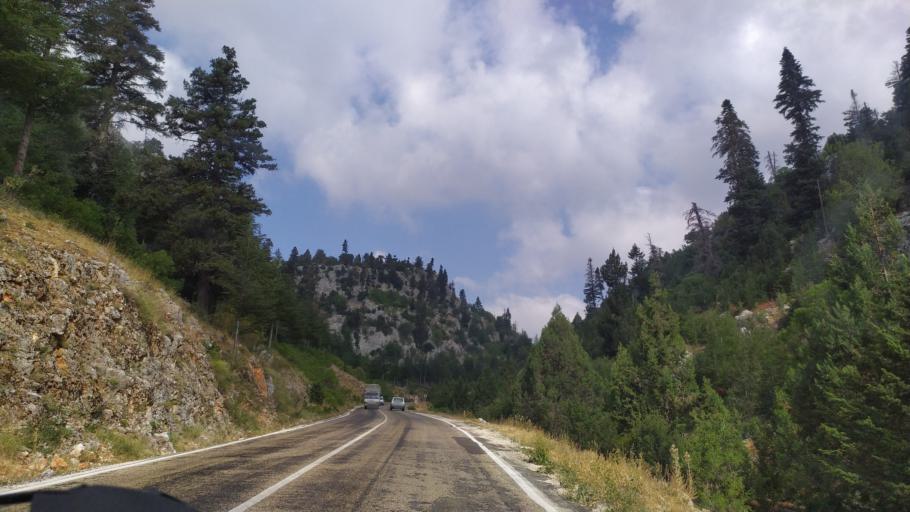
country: TR
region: Mersin
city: Kirobasi
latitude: 36.6033
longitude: 33.8883
